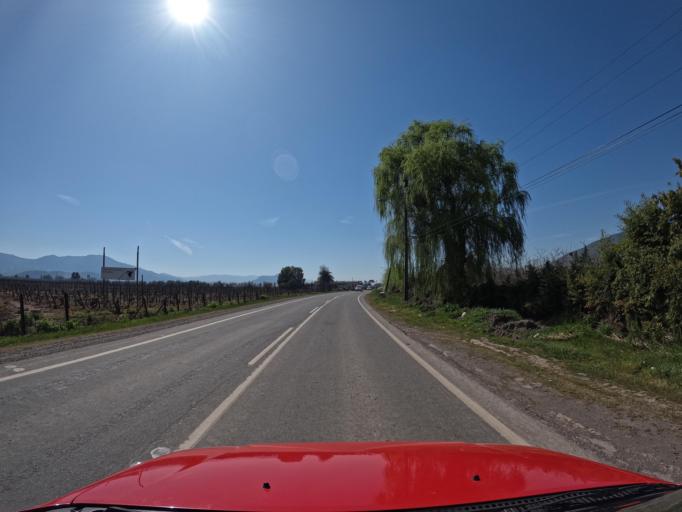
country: CL
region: Maule
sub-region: Provincia de Curico
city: Rauco
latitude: -35.0179
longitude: -71.4257
